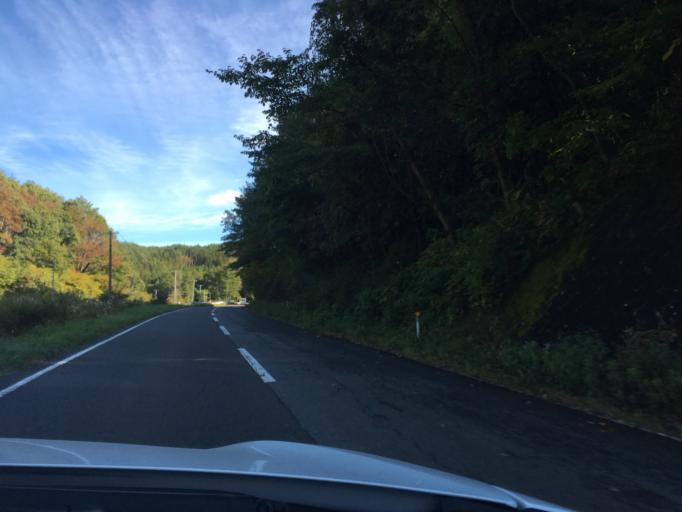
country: JP
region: Fukushima
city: Ishikawa
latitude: 37.1615
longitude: 140.5954
